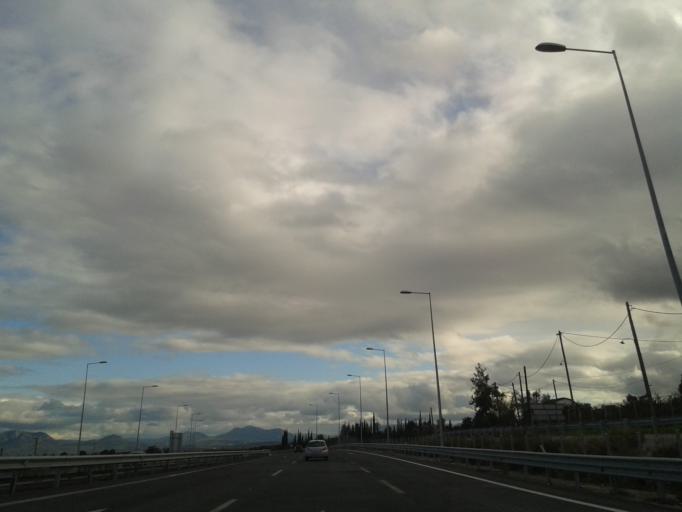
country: GR
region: Peloponnese
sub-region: Nomos Korinthias
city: Velo
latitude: 37.9731
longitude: 22.7420
